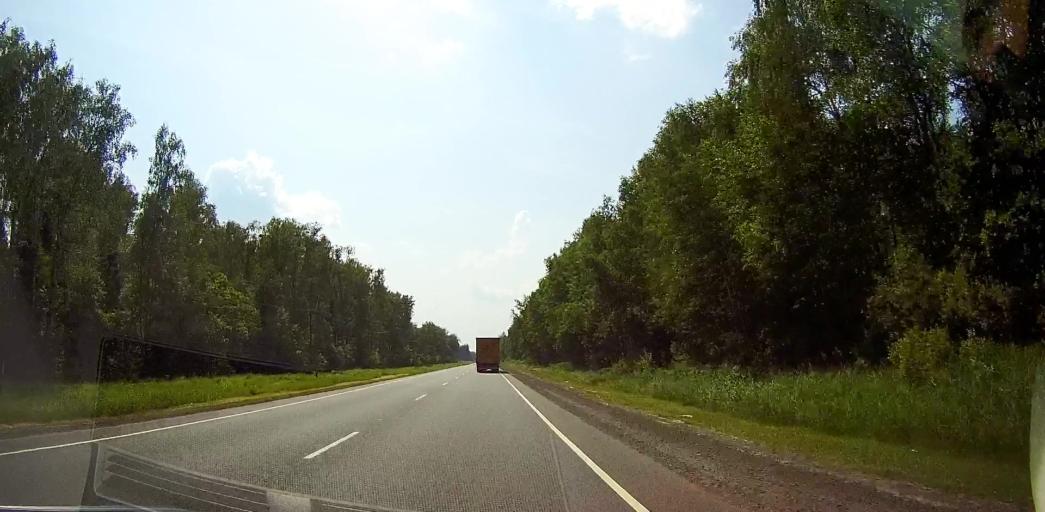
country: RU
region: Moskovskaya
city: Meshcherino
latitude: 55.2106
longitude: 38.3860
